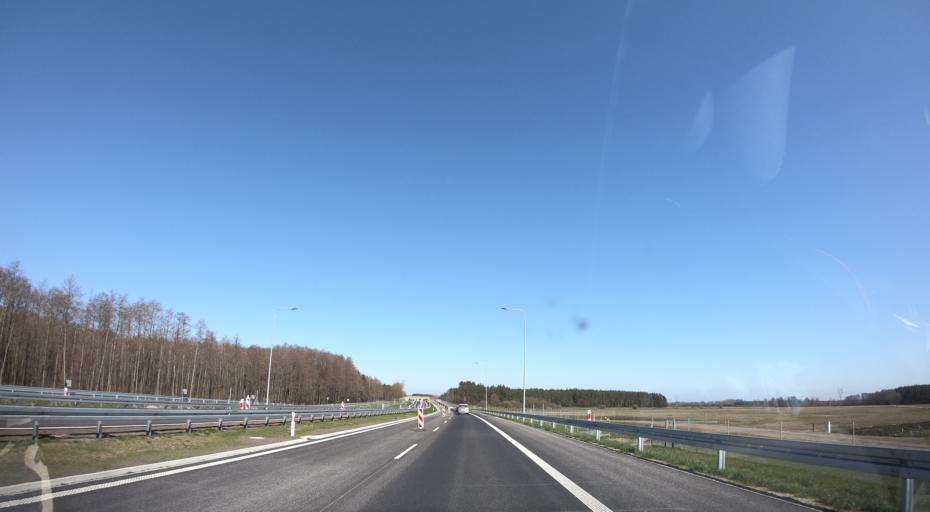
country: PL
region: West Pomeranian Voivodeship
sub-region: Powiat goleniowski
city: Przybiernow
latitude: 53.7723
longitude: 14.7810
